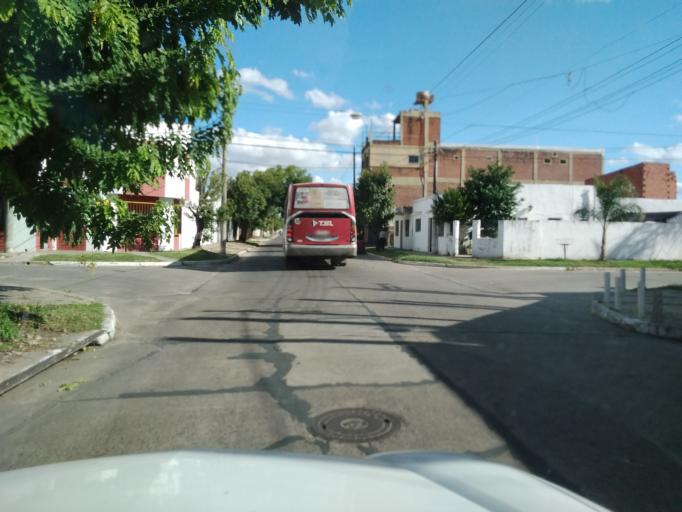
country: AR
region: Corrientes
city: Corrientes
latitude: -27.4913
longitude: -58.8332
